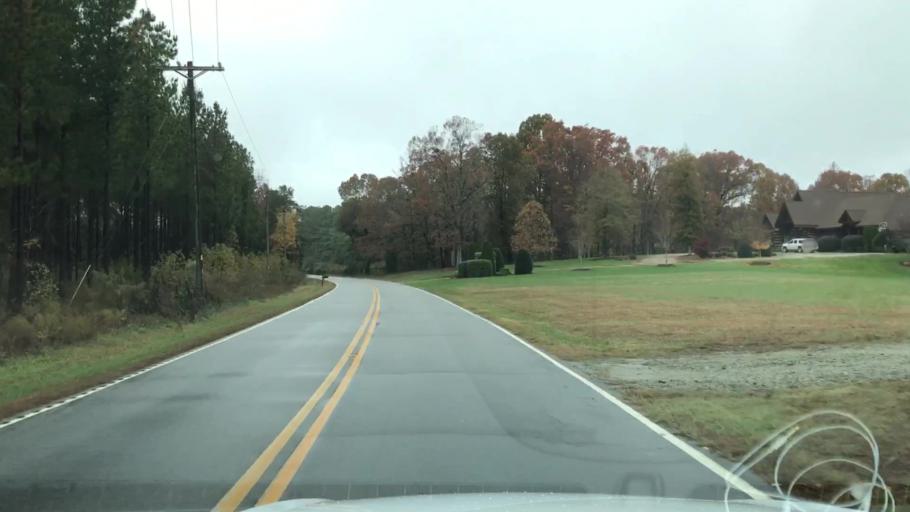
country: US
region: South Carolina
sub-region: Spartanburg County
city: Roebuck
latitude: 34.7771
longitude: -81.9098
